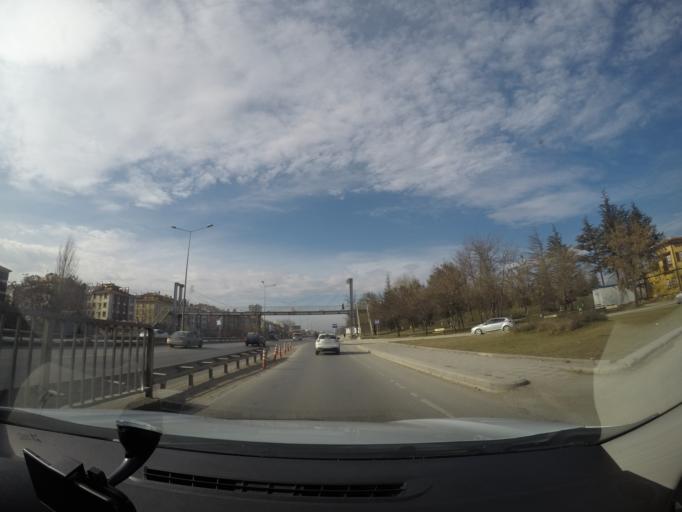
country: TR
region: Eskisehir
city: Eskisehir
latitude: 39.7928
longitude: 30.5106
